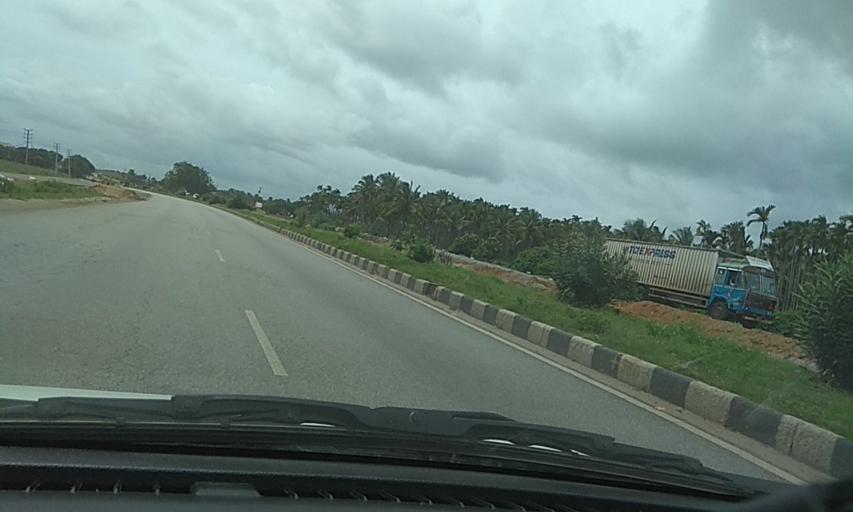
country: IN
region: Karnataka
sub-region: Davanagere
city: Mayakonda
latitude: 14.3419
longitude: 76.2076
